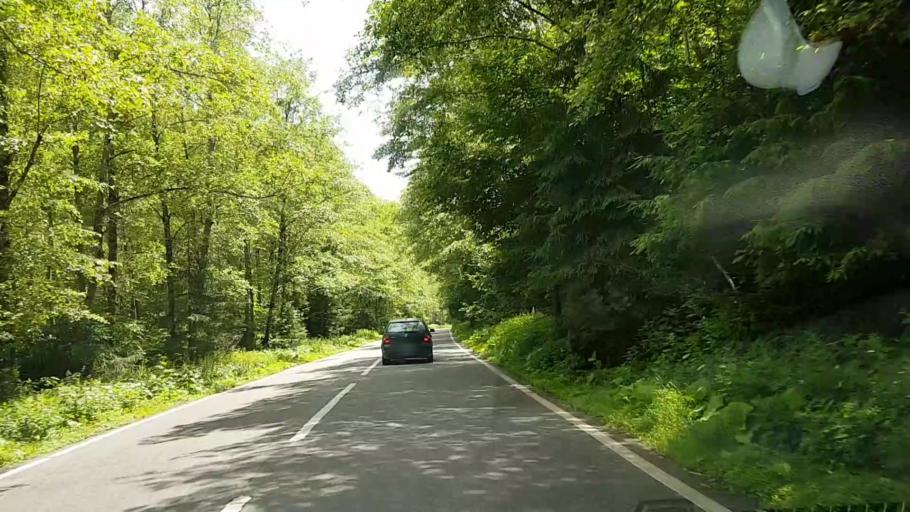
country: RO
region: Suceava
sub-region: Comuna Crucea
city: Crucea
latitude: 47.2891
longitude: 25.6340
